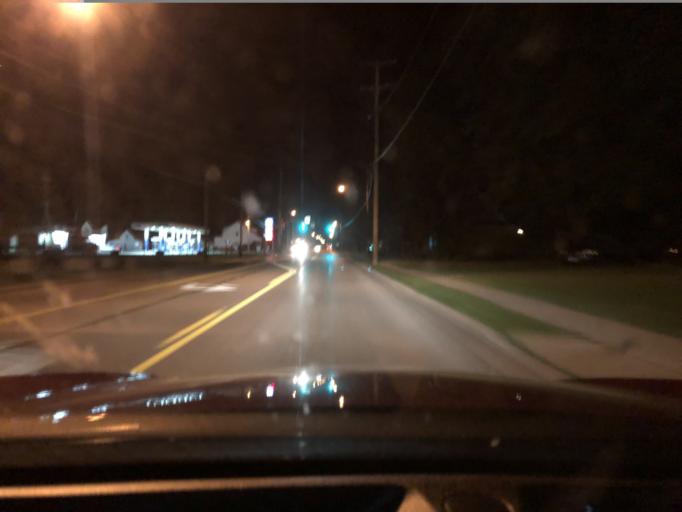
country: US
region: Ohio
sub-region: Van Wert County
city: Van Wert
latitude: 40.8820
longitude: -84.5832
